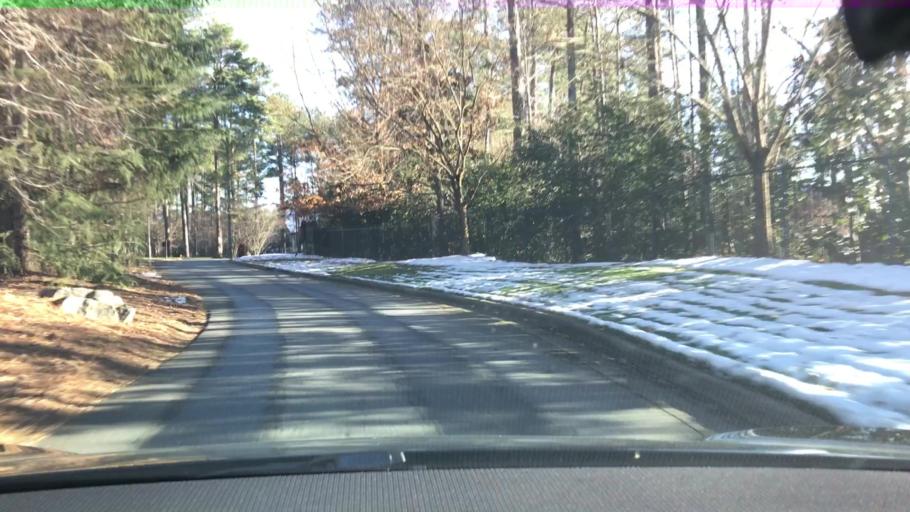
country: US
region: Georgia
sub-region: Gwinnett County
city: Suwanee
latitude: 34.0702
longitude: -84.0927
